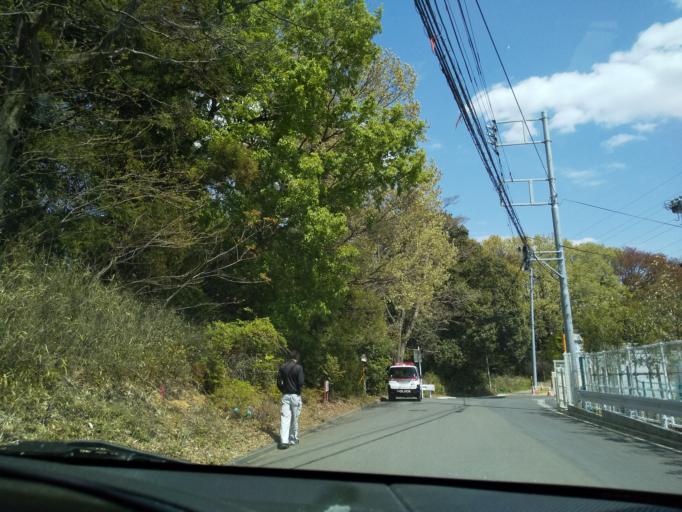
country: JP
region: Tokyo
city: Hino
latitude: 35.5989
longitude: 139.3889
